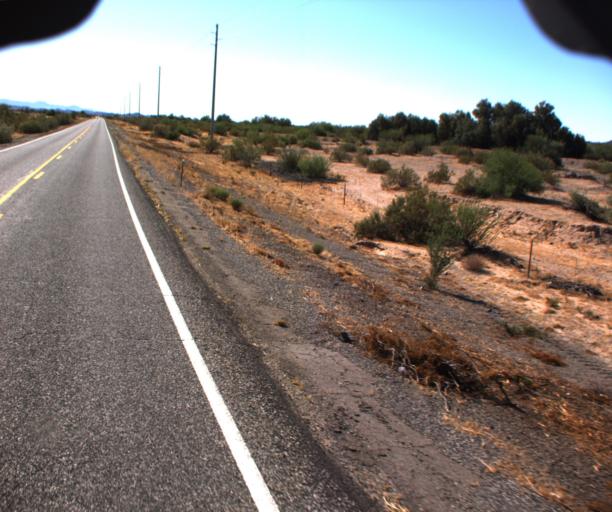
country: US
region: Arizona
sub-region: La Paz County
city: Cienega Springs
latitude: 33.9905
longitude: -114.0786
